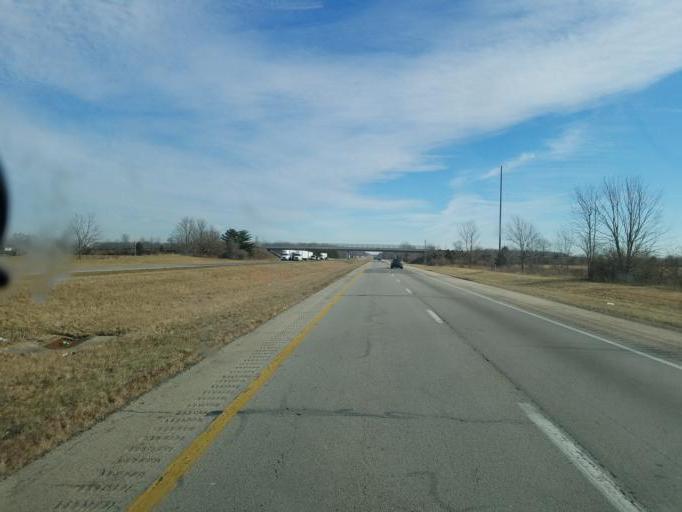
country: US
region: Ohio
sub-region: Preble County
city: New Paris
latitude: 39.8354
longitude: -84.7002
